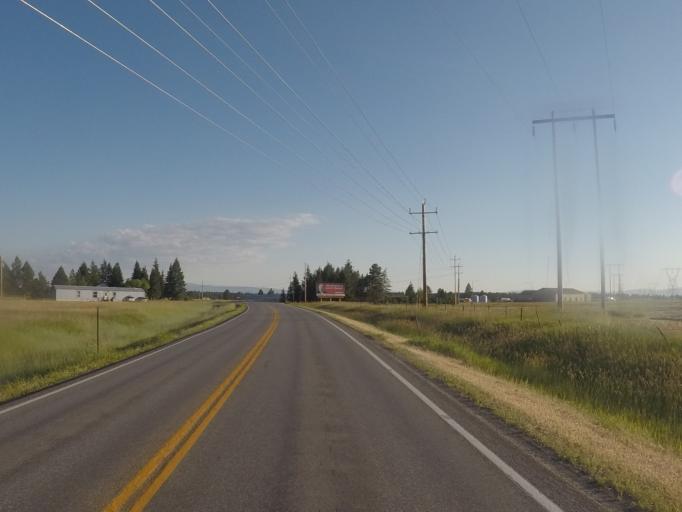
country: US
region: Montana
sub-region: Flathead County
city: Columbia Falls
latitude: 48.3576
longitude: -114.1572
